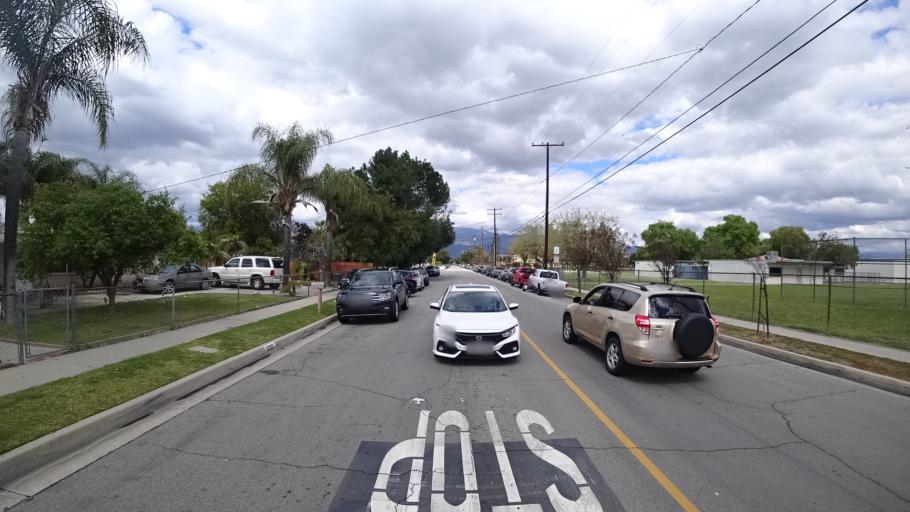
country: US
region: California
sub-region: Los Angeles County
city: Baldwin Park
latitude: 34.0886
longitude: -117.9758
